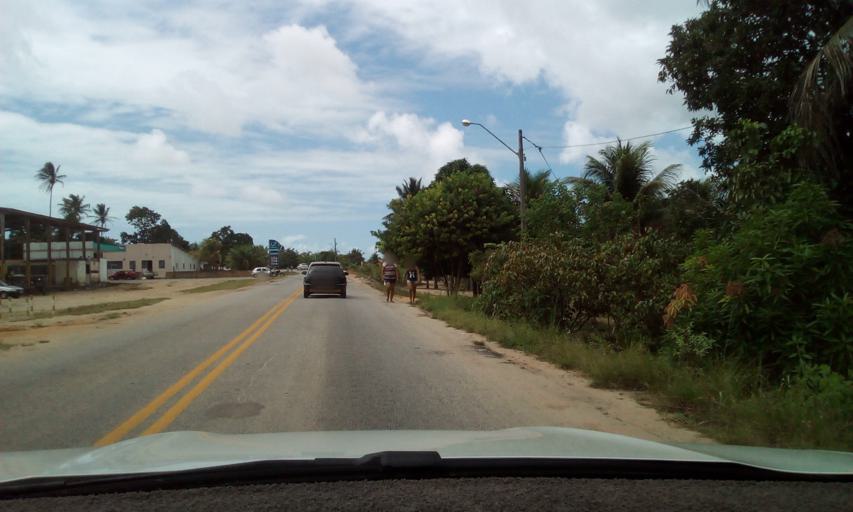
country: BR
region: Paraiba
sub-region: Rio Tinto
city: Rio Tinto
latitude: -6.7714
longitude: -35.0125
